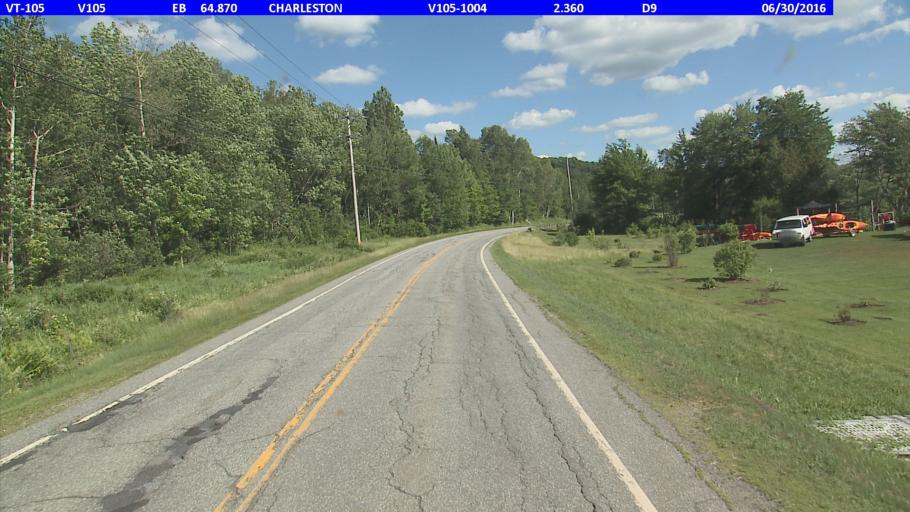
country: US
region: Vermont
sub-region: Orleans County
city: Newport
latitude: 44.8821
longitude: -72.0526
